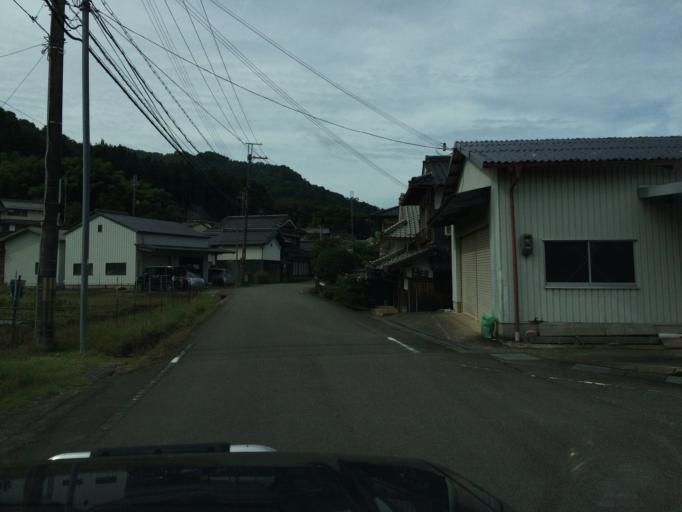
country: JP
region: Hyogo
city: Sasayama
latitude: 35.0722
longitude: 135.3612
